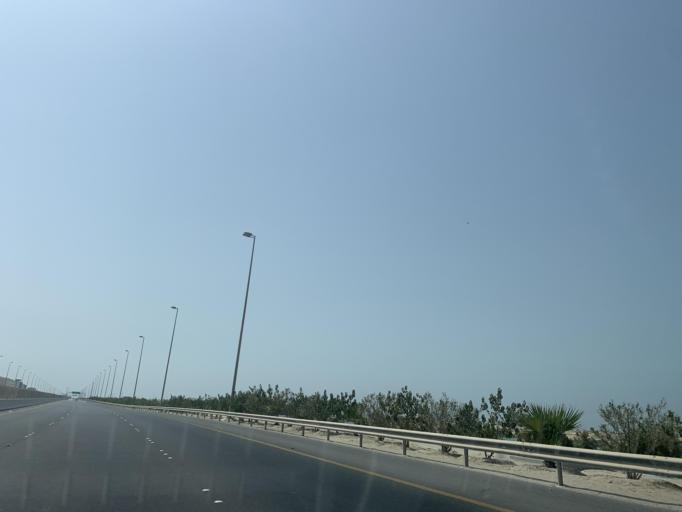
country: BH
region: Muharraq
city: Al Hadd
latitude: 26.2787
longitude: 50.6560
